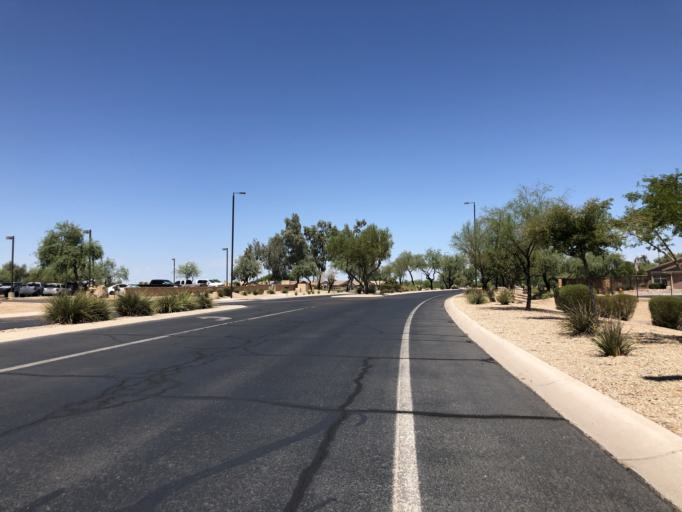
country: US
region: Arizona
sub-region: Maricopa County
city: Sun Lakes
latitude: 33.2157
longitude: -111.7827
